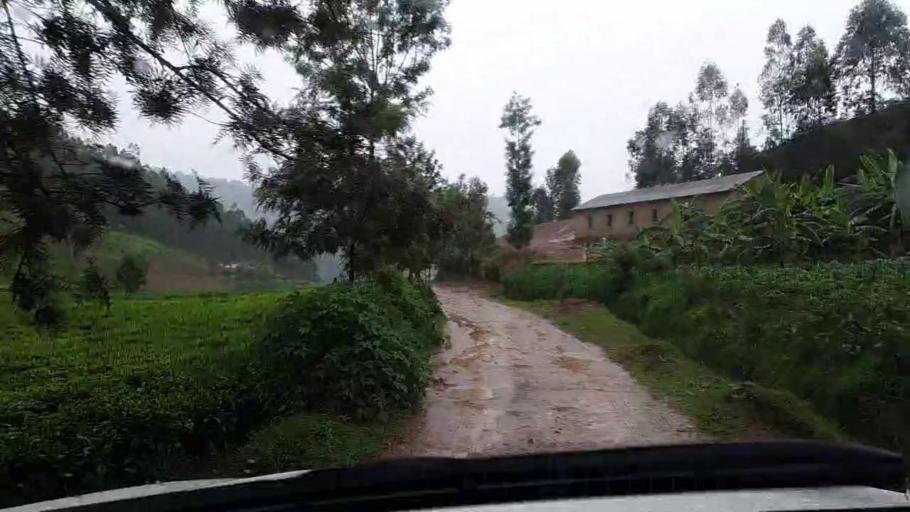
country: RW
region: Northern Province
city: Byumba
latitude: -1.6522
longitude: 29.9159
